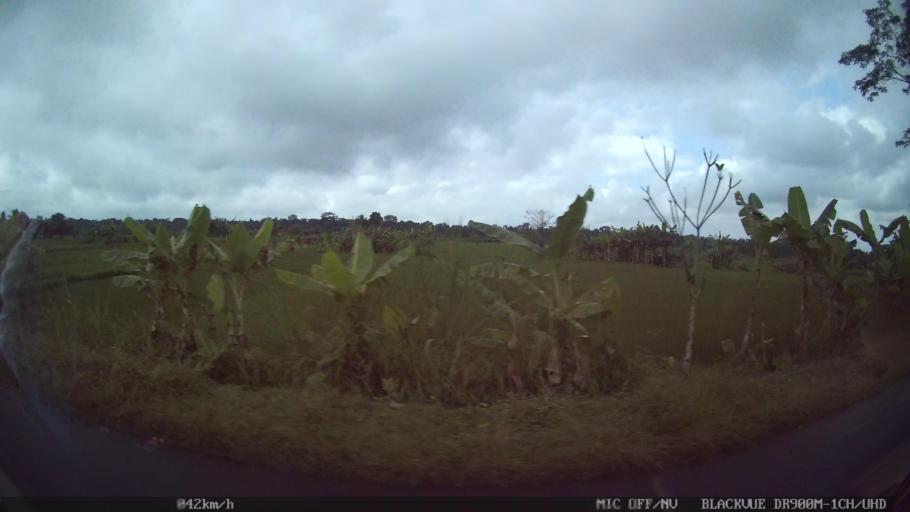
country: ID
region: Bali
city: Banjar Teguan
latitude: -8.5009
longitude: 115.2255
